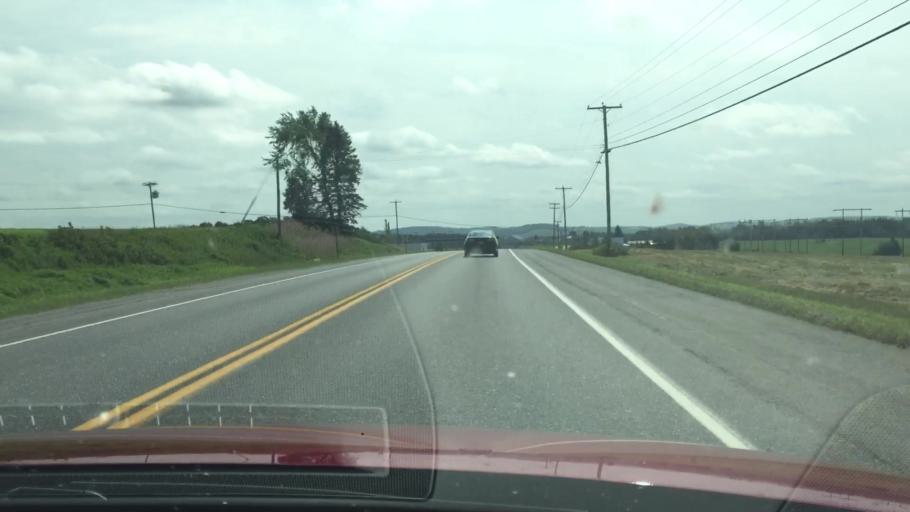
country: US
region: Maine
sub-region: Aroostook County
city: Easton
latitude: 46.4545
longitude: -67.8544
